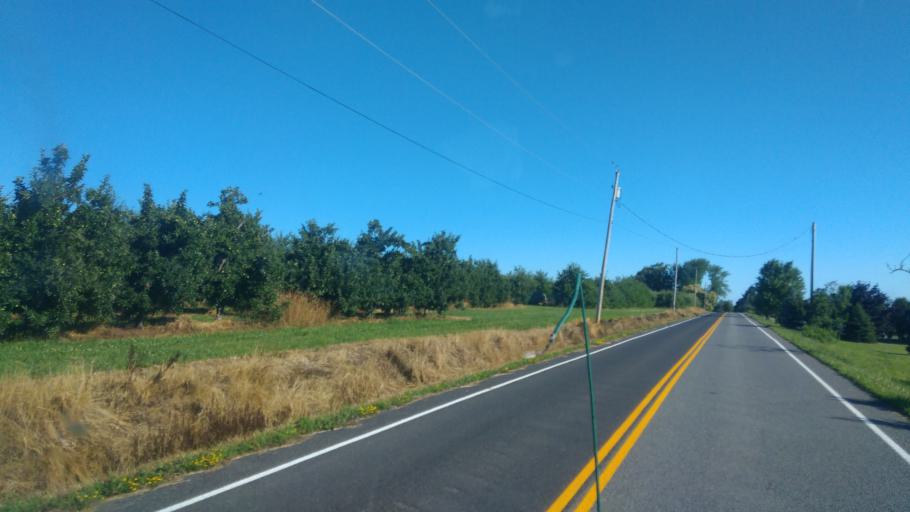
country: US
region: New York
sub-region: Wayne County
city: Sodus
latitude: 43.2035
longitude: -77.1030
